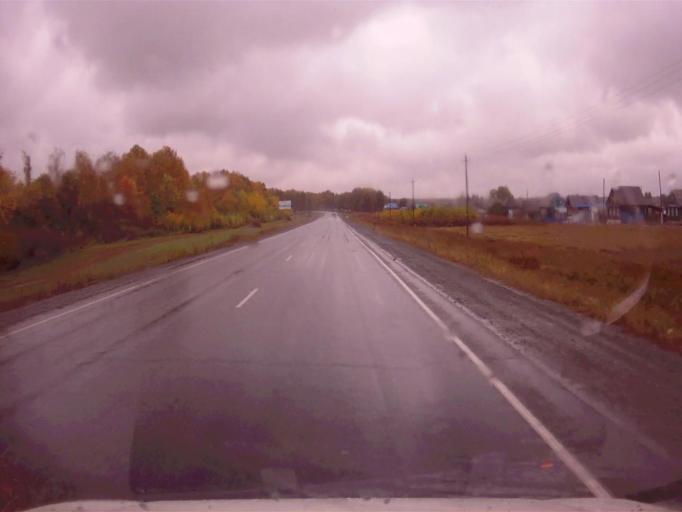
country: RU
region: Chelyabinsk
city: Argayash
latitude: 55.4076
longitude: 61.0554
